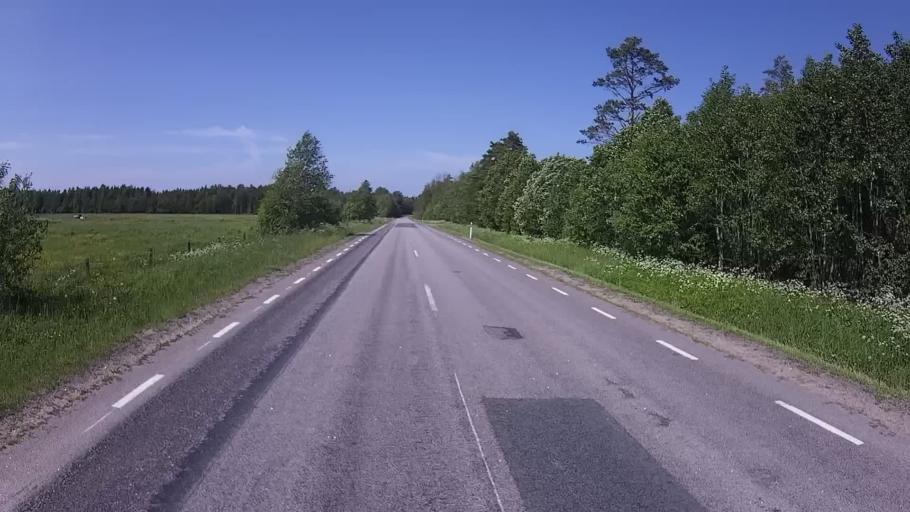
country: EE
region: Saare
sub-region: Kuressaare linn
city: Kuressaare
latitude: 58.4002
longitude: 22.4295
